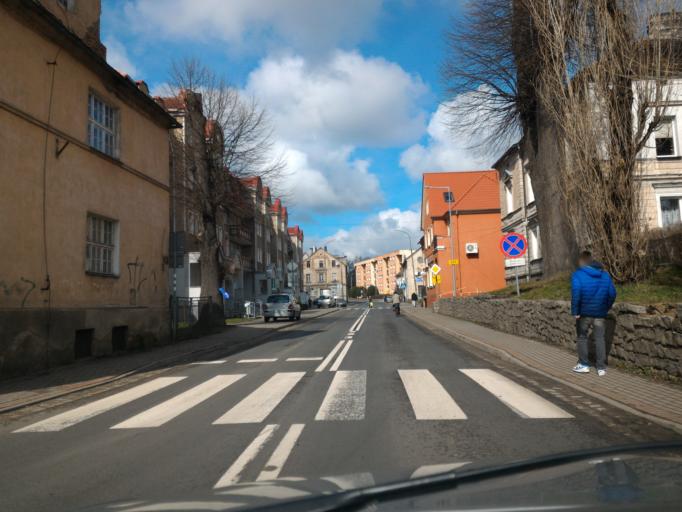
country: PL
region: Silesian Voivodeship
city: Zawidow
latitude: 51.0255
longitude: 15.0622
